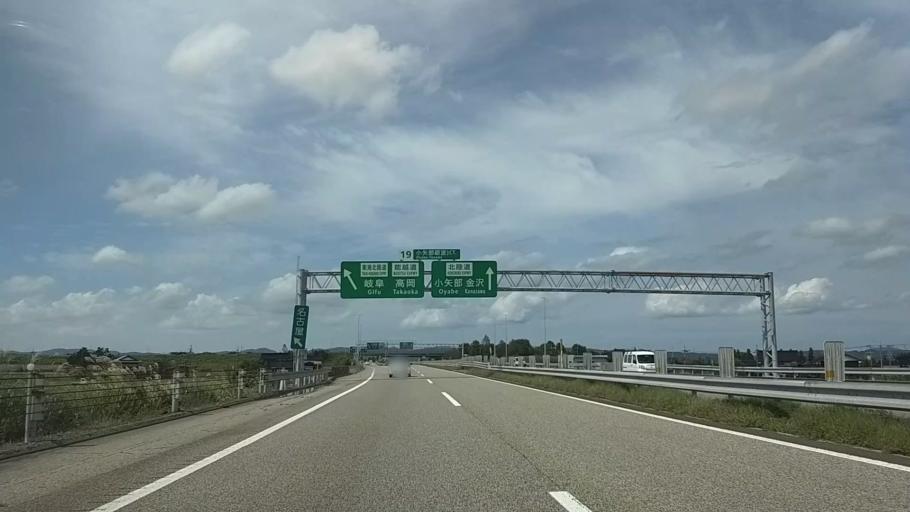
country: JP
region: Toyama
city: Nanto-shi
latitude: 36.6290
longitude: 136.9148
